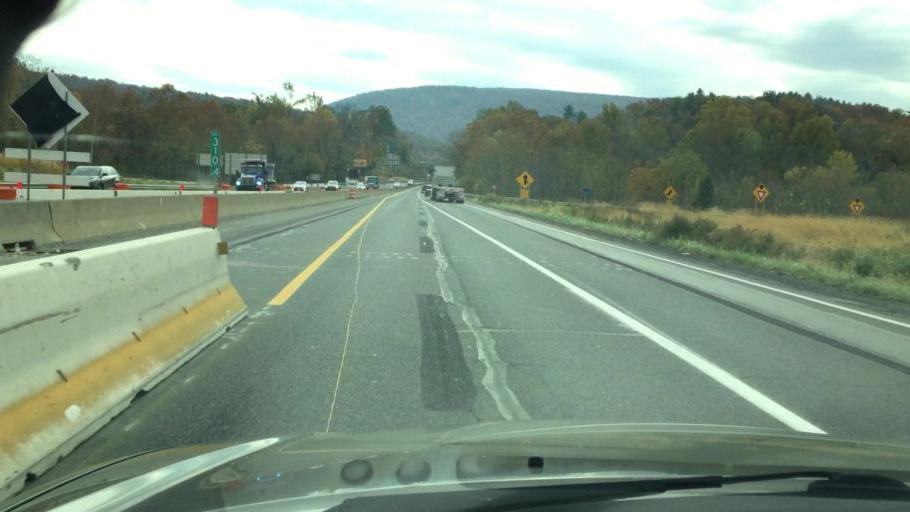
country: US
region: Pennsylvania
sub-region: Monroe County
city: East Stroudsburg
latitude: 40.9887
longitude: -75.1398
